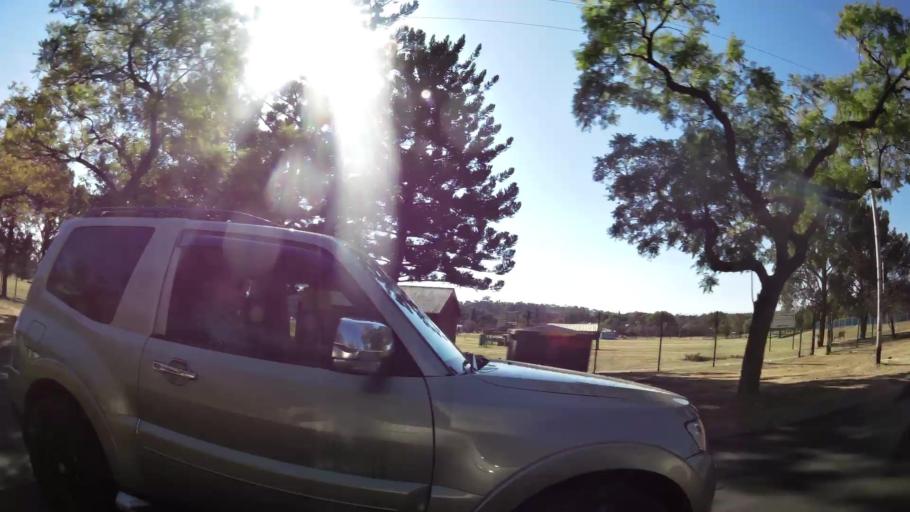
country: ZA
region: Gauteng
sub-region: City of Tshwane Metropolitan Municipality
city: Pretoria
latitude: -25.7338
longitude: 28.2235
